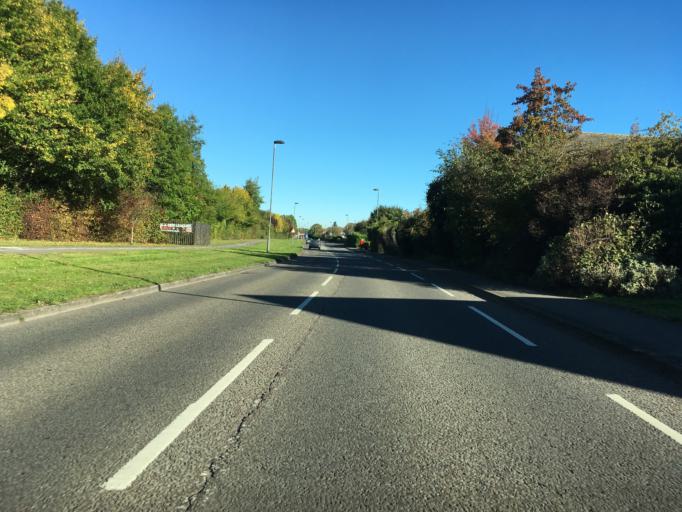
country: GB
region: England
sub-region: South Gloucestershire
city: Yate
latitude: 51.5344
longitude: -2.4093
